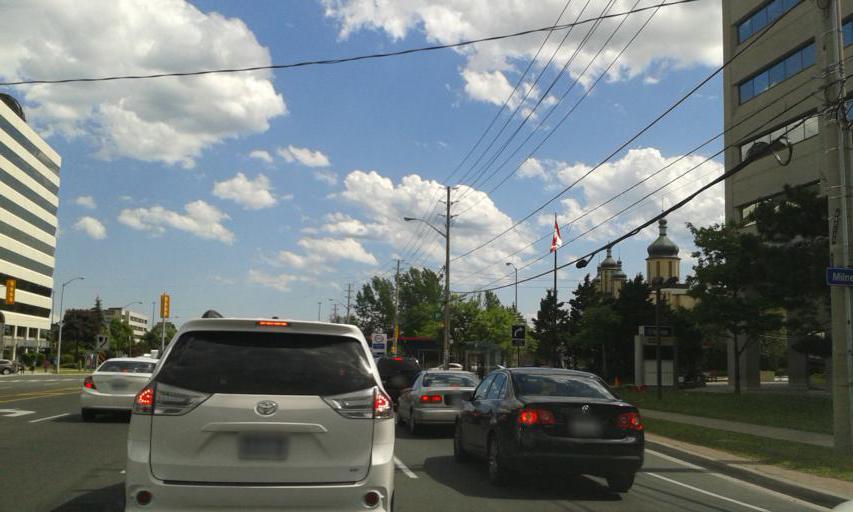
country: CA
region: Ontario
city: Scarborough
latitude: 43.7904
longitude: -79.2375
